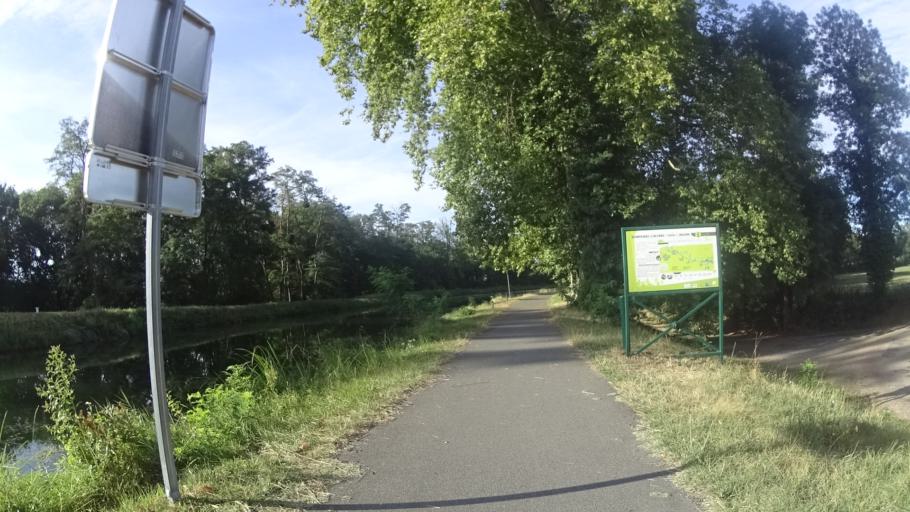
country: FR
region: Bourgogne
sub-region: Departement de Saone-et-Loire
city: Digoin
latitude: 46.4742
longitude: 3.9784
